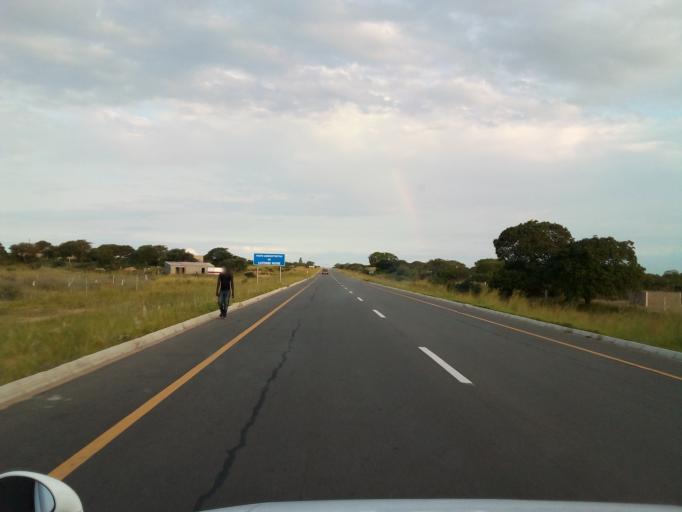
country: MZ
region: Maputo City
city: Maputo
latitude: -26.0564
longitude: 32.5873
